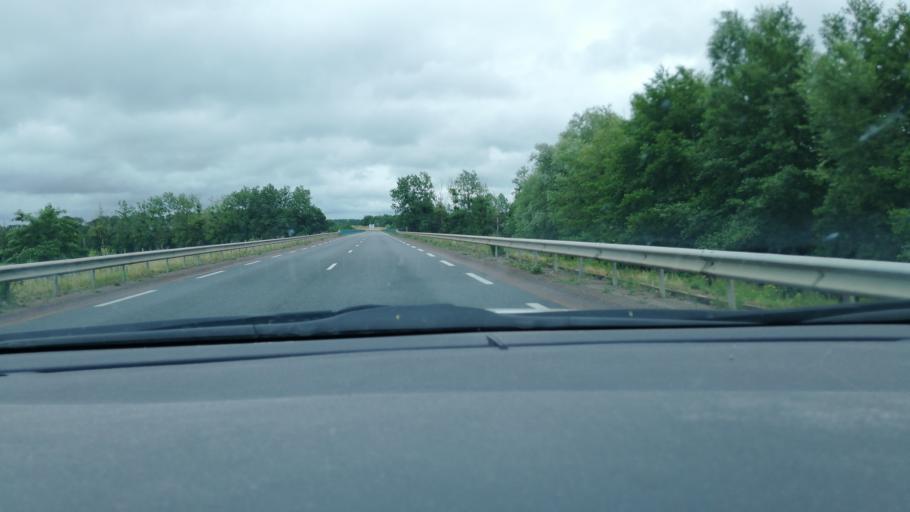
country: FR
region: Poitou-Charentes
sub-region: Departement de la Vienne
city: Cenon-sur-Vienne
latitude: 46.7825
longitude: 0.5378
